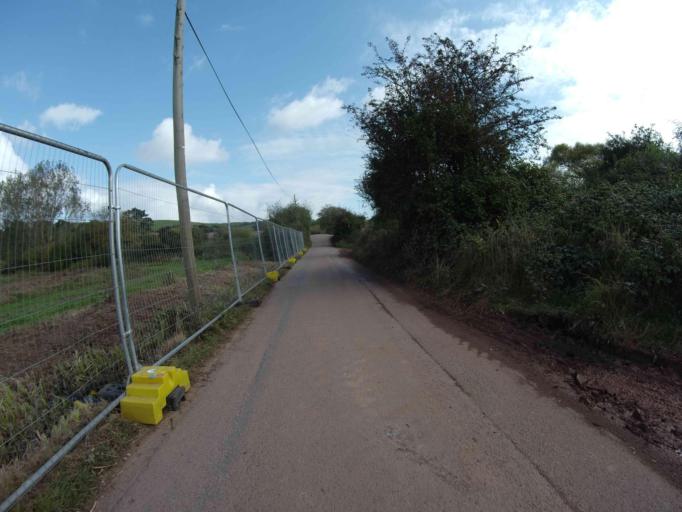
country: GB
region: England
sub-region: Devon
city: Budleigh Salterton
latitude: 50.6396
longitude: -3.3106
